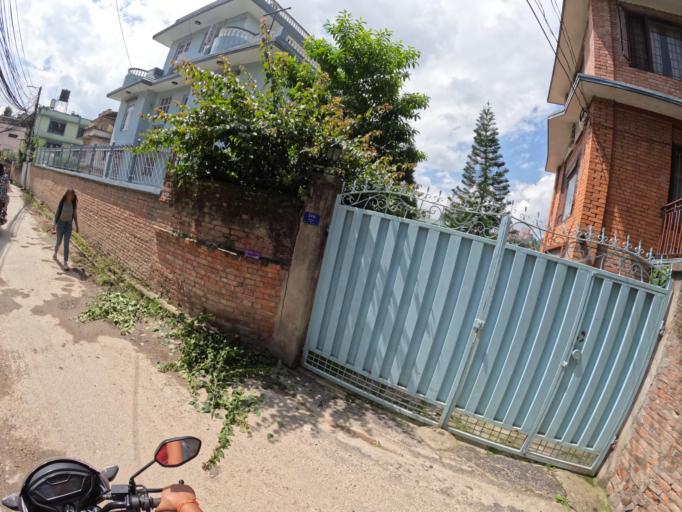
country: NP
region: Central Region
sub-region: Bagmati Zone
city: Patan
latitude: 27.6810
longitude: 85.3093
